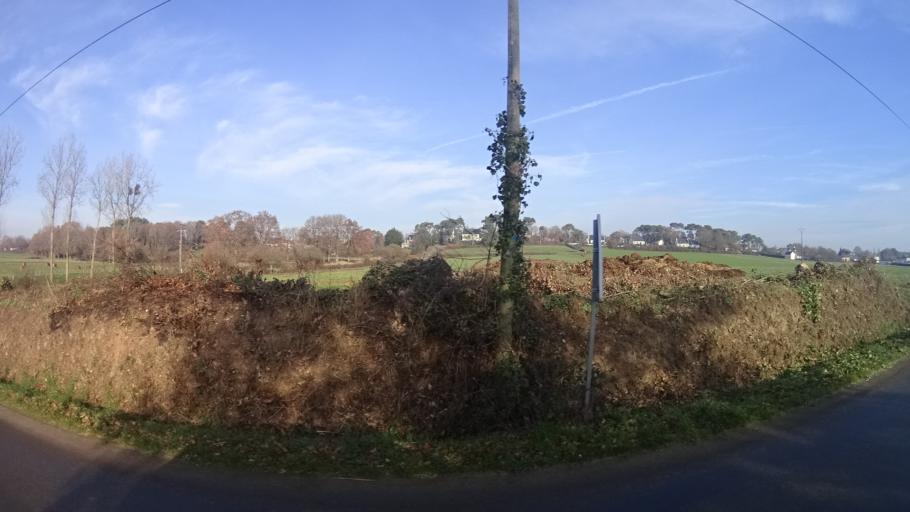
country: FR
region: Brittany
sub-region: Departement du Morbihan
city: Rieux
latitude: 47.5985
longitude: -2.1212
